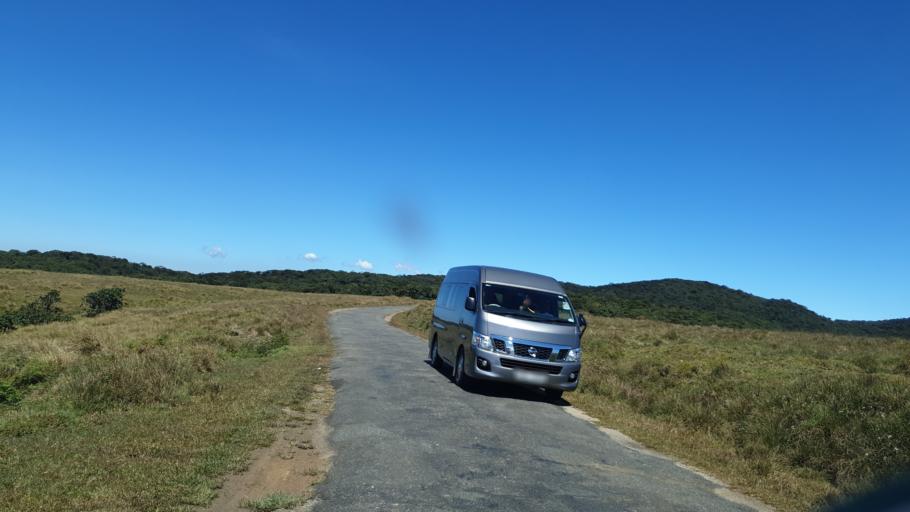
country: LK
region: Central
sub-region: Nuwara Eliya District
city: Nuwara Eliya
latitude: 6.8218
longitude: 80.8058
